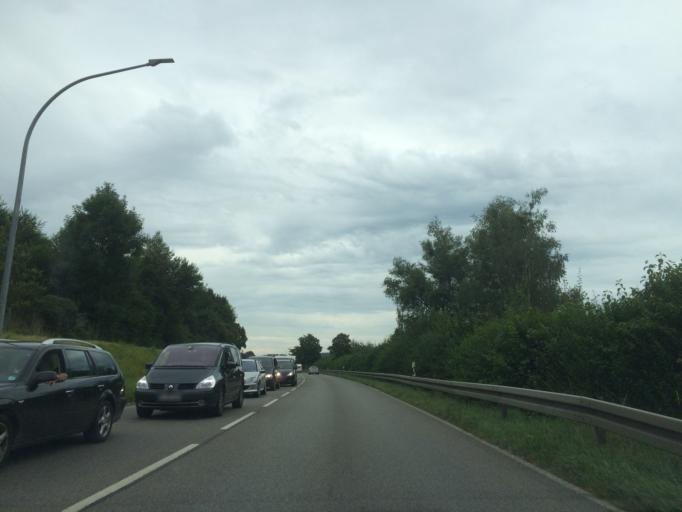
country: DE
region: Baden-Wuerttemberg
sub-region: Tuebingen Region
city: Markdorf
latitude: 47.7181
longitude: 9.3986
